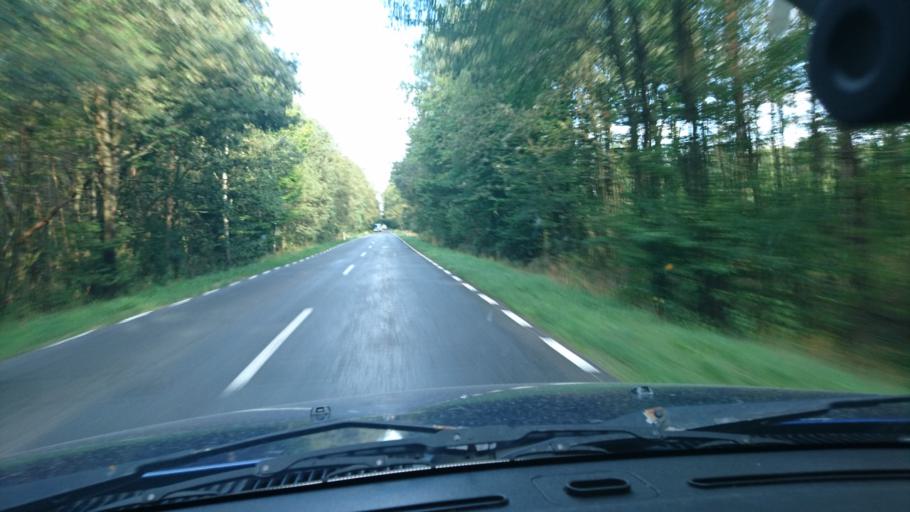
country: PL
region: Greater Poland Voivodeship
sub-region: Powiat krotoszynski
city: Sulmierzyce
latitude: 51.5998
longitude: 17.5972
